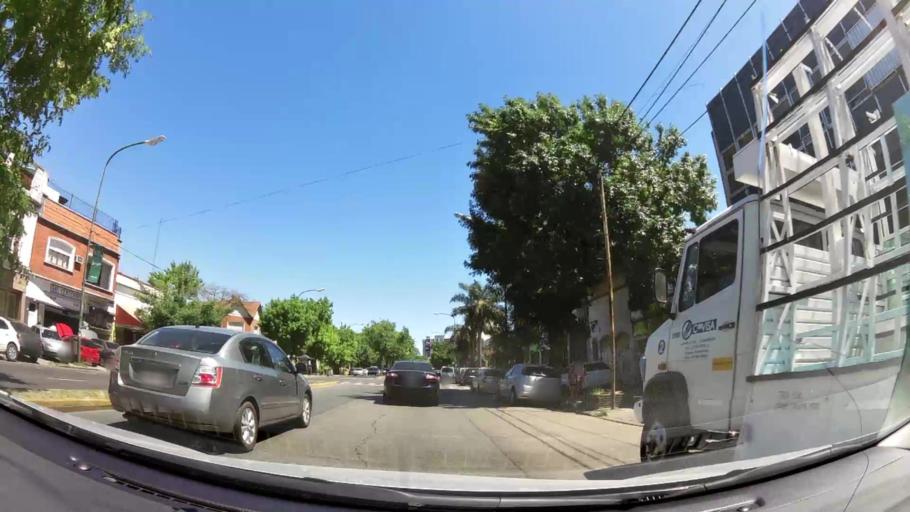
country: AR
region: Buenos Aires
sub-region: Partido de San Isidro
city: San Isidro
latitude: -34.4663
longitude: -58.5205
